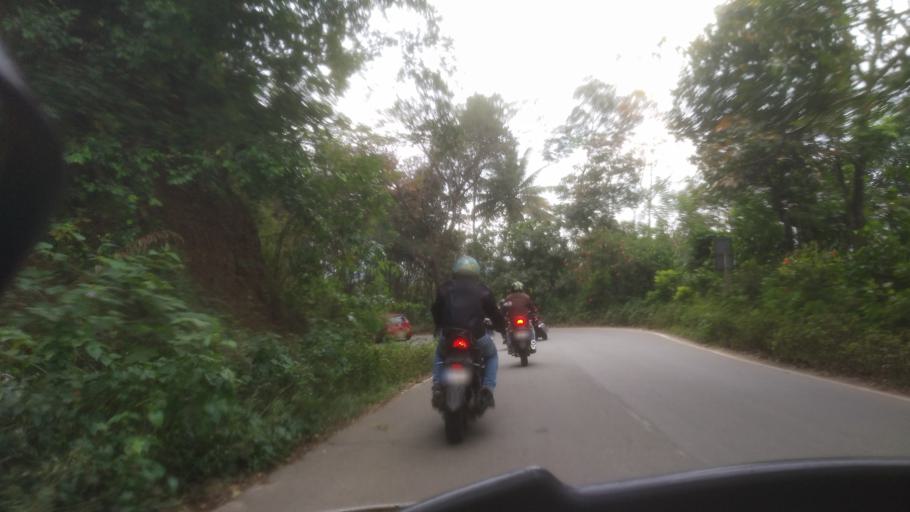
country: IN
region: Kerala
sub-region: Idukki
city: Munnar
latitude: 9.9814
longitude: 76.9919
